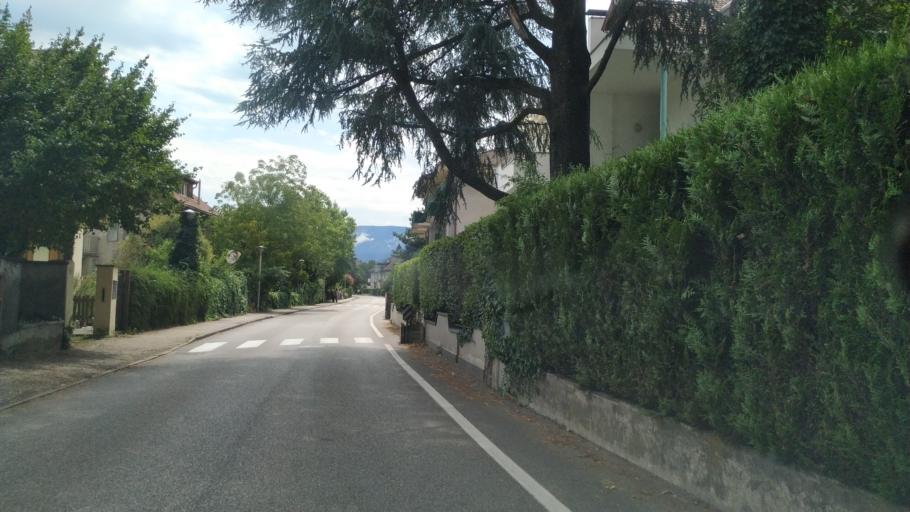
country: IT
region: Trentino-Alto Adige
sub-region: Bolzano
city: Tirolo
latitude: 46.6793
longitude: 11.1477
